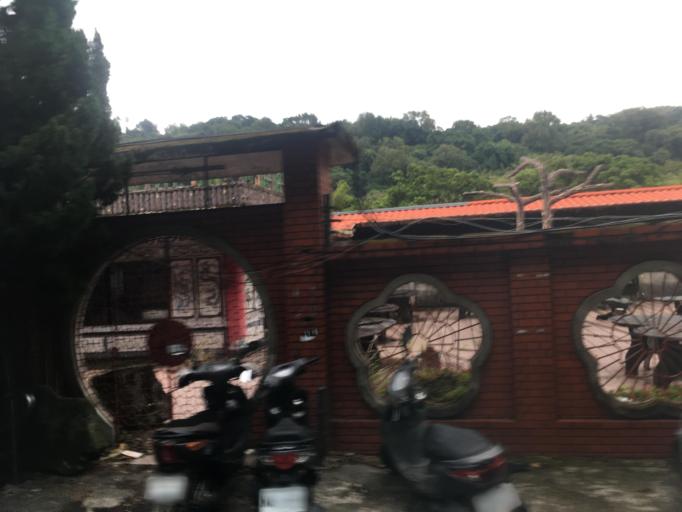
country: TW
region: Taipei
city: Taipei
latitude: 25.1483
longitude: 121.5308
